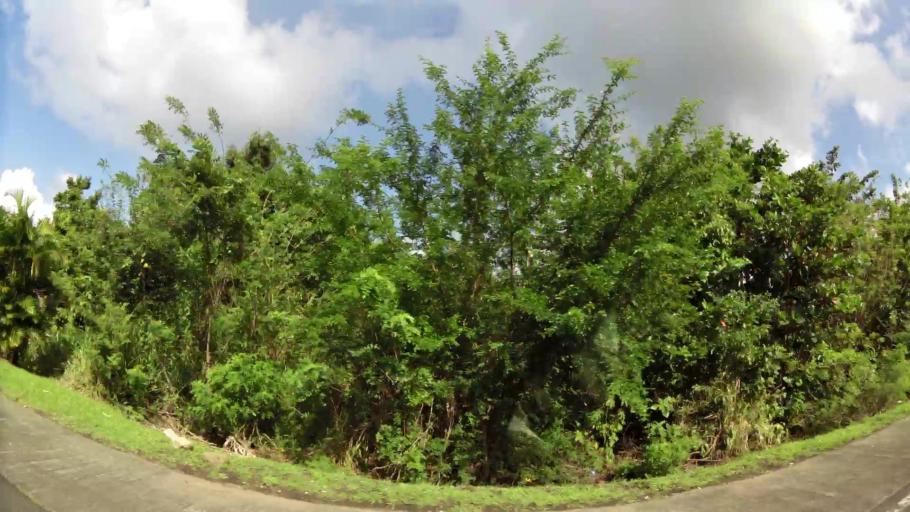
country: MQ
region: Martinique
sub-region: Martinique
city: Les Trois-Ilets
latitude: 14.5348
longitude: -61.0287
